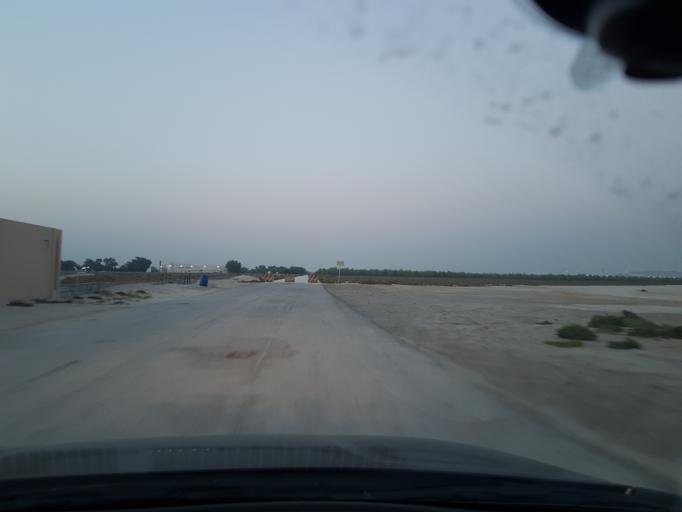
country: BH
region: Central Governorate
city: Dar Kulayb
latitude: 26.0089
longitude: 50.4755
